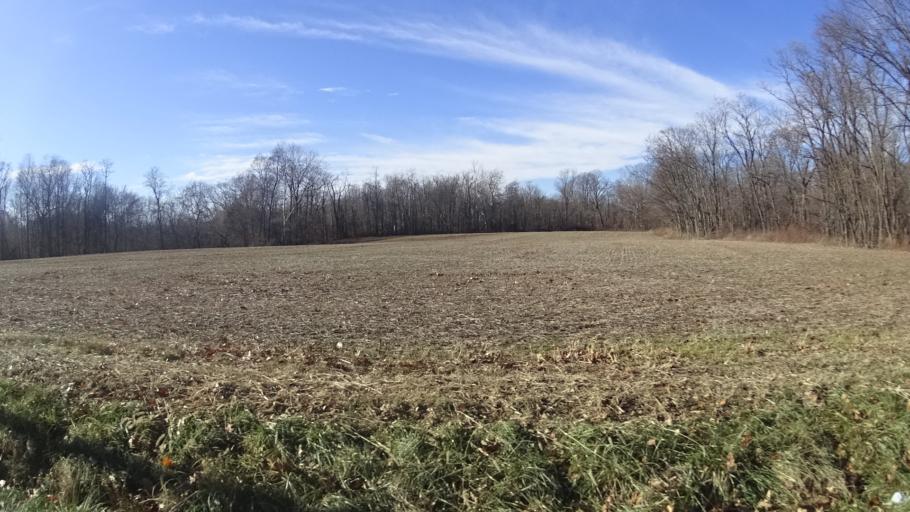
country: US
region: Ohio
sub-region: Huron County
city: Wakeman
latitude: 41.3067
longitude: -82.3432
